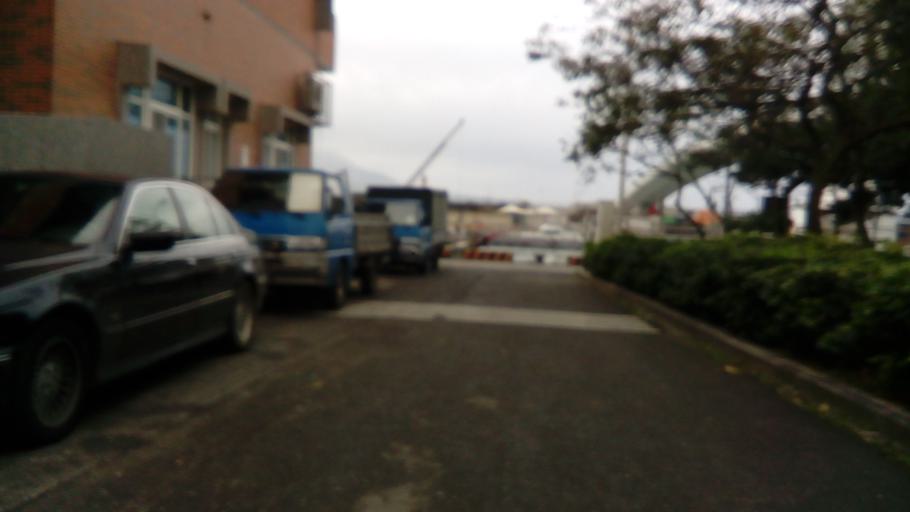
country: TW
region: Taipei
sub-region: Taipei
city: Banqiao
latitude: 25.1838
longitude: 121.4112
